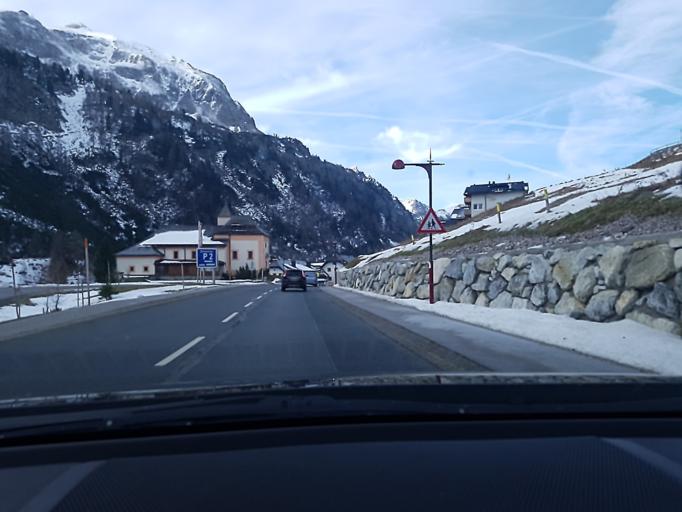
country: AT
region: Salzburg
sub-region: Politischer Bezirk Sankt Johann im Pongau
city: Untertauern
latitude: 47.2510
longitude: 13.5411
